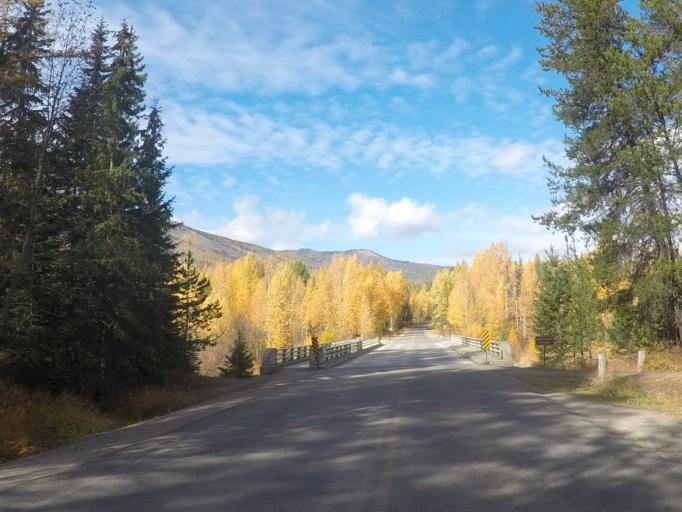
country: US
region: Montana
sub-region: Flathead County
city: Columbia Falls
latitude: 48.5256
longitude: -113.9962
